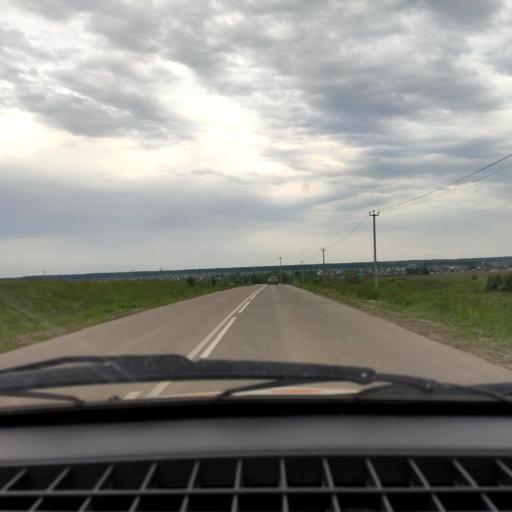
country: RU
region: Bashkortostan
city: Avdon
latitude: 54.5633
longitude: 55.7608
